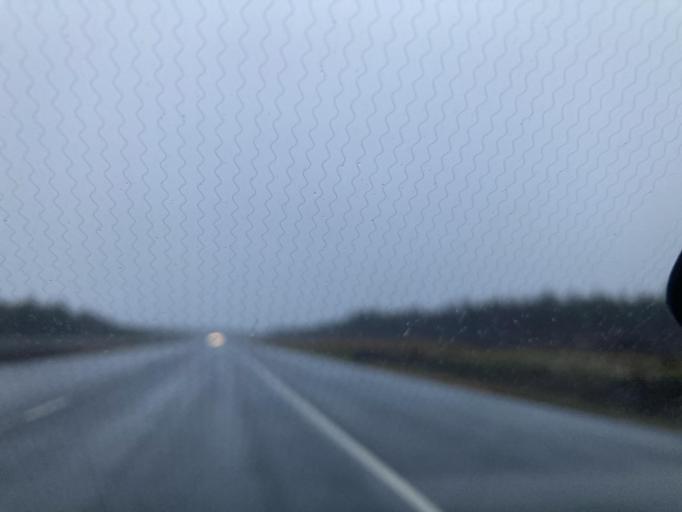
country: FI
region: Lapland
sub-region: Rovaniemi
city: Rovaniemi
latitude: 66.5696
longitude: 25.7973
